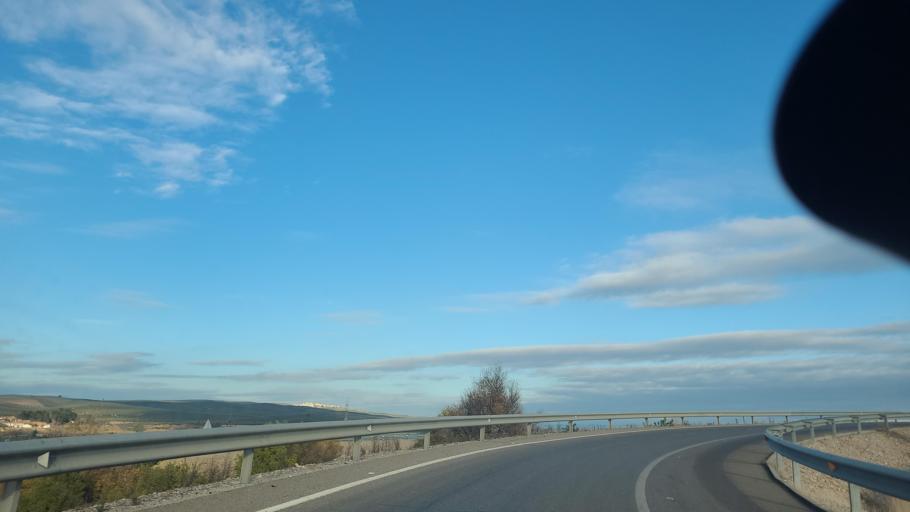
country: ES
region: Andalusia
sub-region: Provincia de Jaen
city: Mengibar
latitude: 37.9763
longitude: -3.7929
